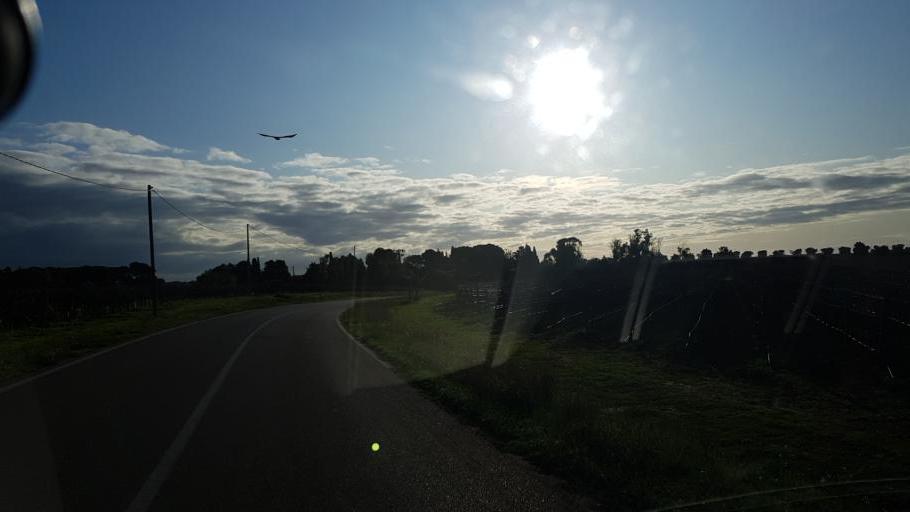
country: IT
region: Apulia
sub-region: Provincia di Brindisi
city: Torchiarolo
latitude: 40.5485
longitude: 18.0411
